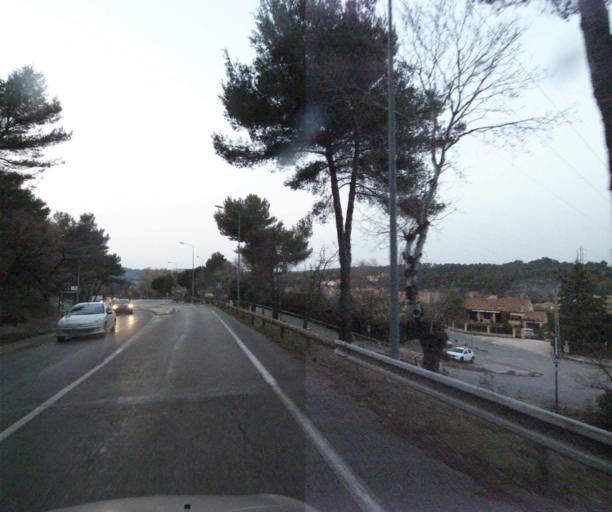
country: FR
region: Provence-Alpes-Cote d'Azur
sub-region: Departement des Bouches-du-Rhone
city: Gardanne
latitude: 43.4267
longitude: 5.4754
